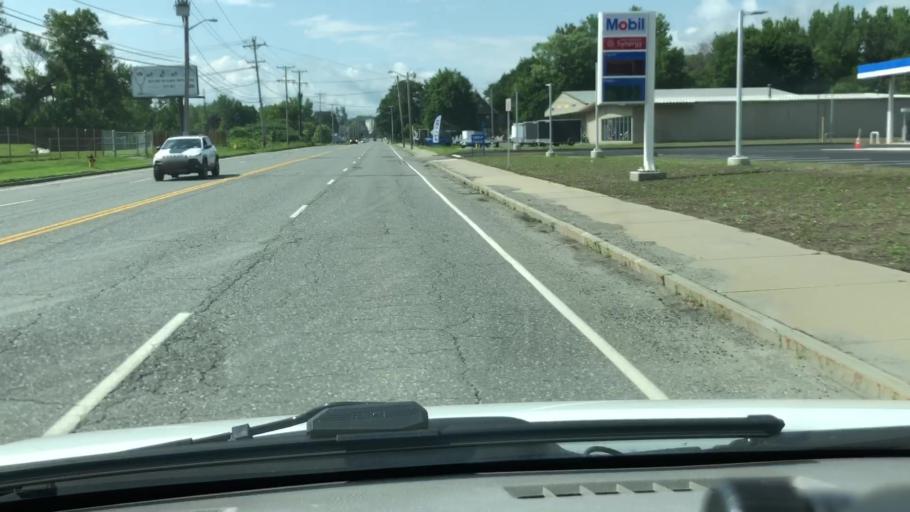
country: US
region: Massachusetts
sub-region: Berkshire County
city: Adams
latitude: 42.6538
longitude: -73.1104
